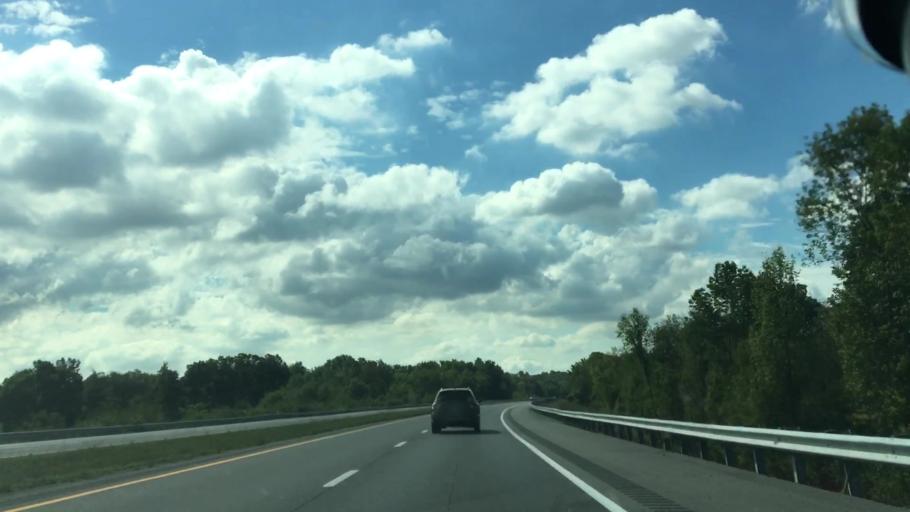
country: US
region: Kentucky
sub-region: Webster County
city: Sebree
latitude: 37.5689
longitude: -87.4781
